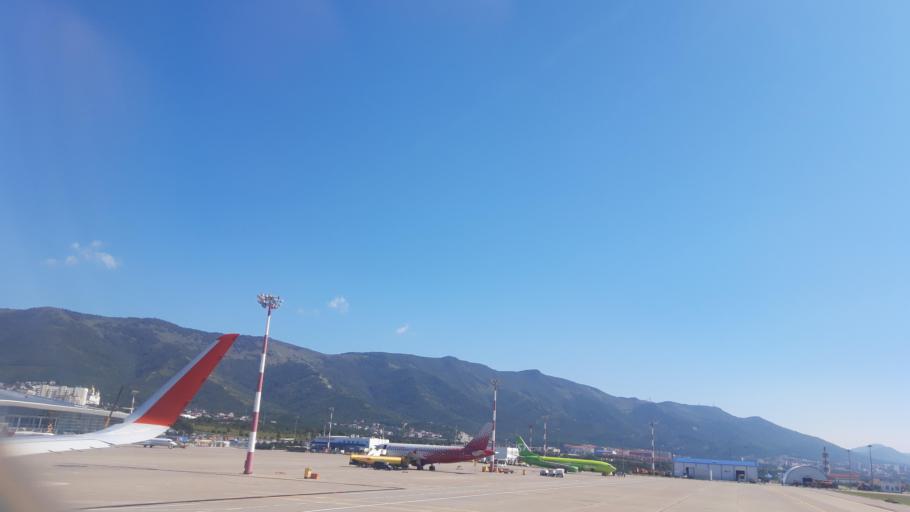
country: RU
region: Krasnodarskiy
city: Gelendzhik
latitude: 44.5927
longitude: 38.0196
